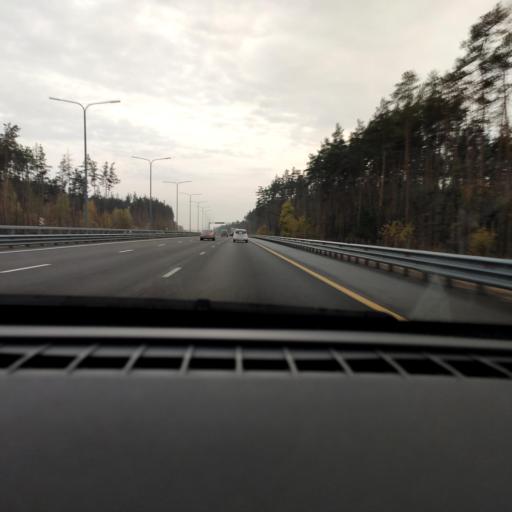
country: RU
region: Voronezj
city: Somovo
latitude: 51.6998
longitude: 39.3060
